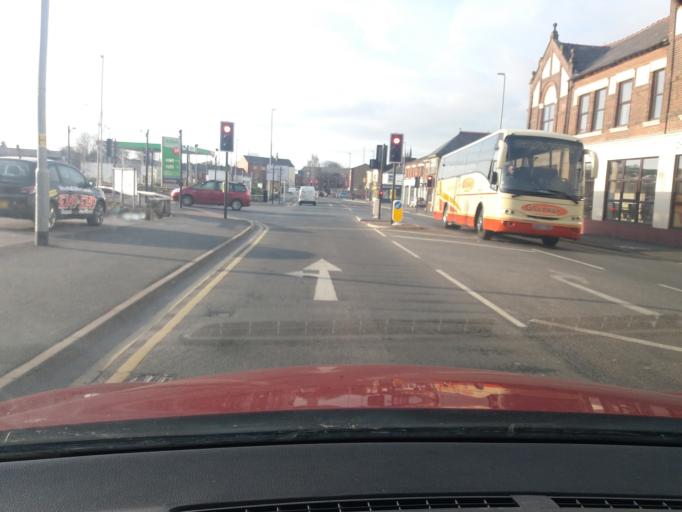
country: GB
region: England
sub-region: Lancashire
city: Chorley
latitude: 53.6490
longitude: -2.6299
